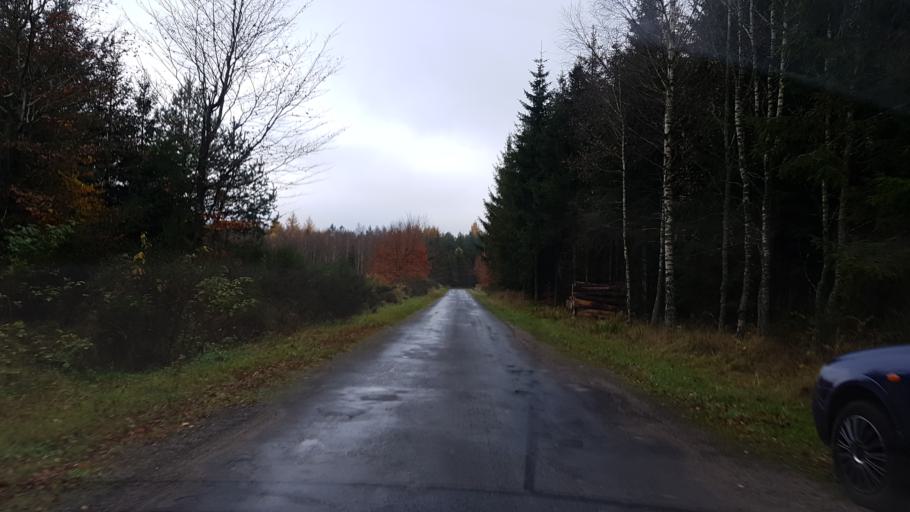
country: PL
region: West Pomeranian Voivodeship
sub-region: Powiat koszalinski
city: Polanow
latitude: 54.0780
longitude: 16.5768
